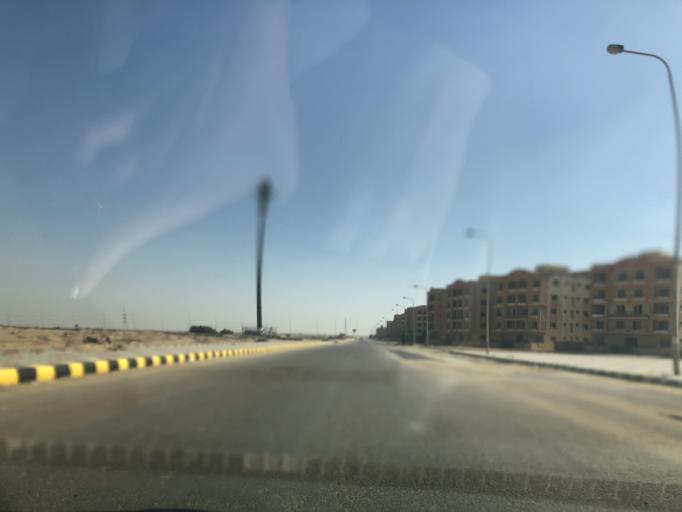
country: EG
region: Al Jizah
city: Madinat Sittah Uktubar
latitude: 29.9037
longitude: 31.0771
